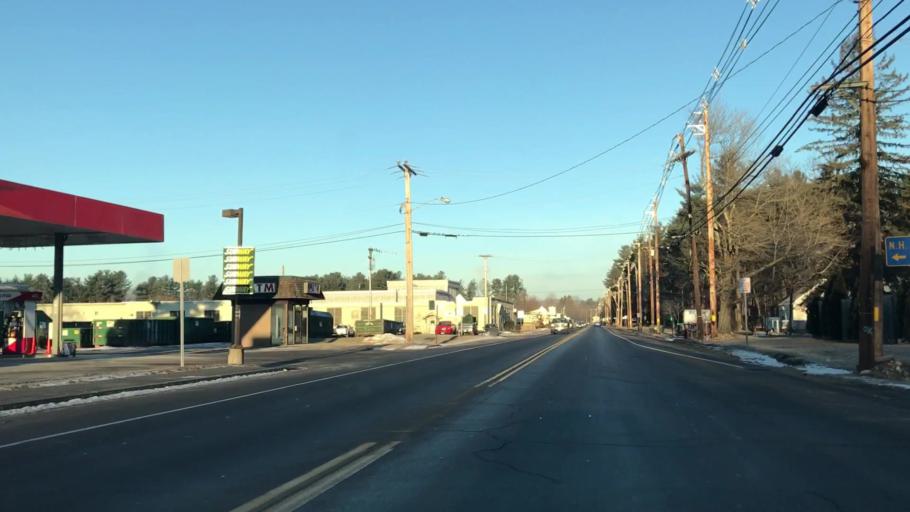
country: US
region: New Hampshire
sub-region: Cheshire County
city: Keene
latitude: 42.9093
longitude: -72.2608
